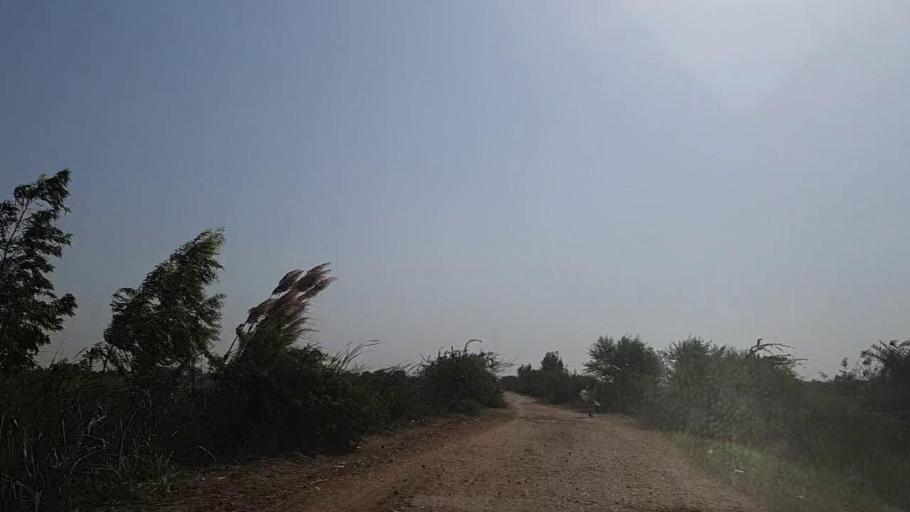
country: PK
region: Sindh
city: Daro Mehar
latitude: 24.7213
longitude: 68.0759
